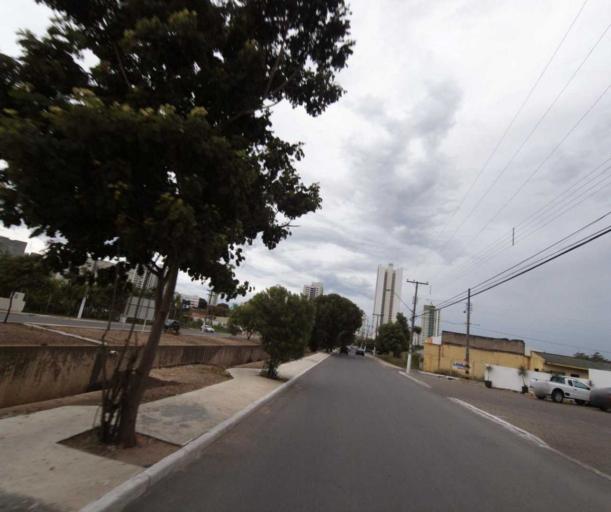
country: BR
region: Mato Grosso
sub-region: Cuiaba
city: Cuiaba
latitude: -15.6187
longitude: -56.0768
